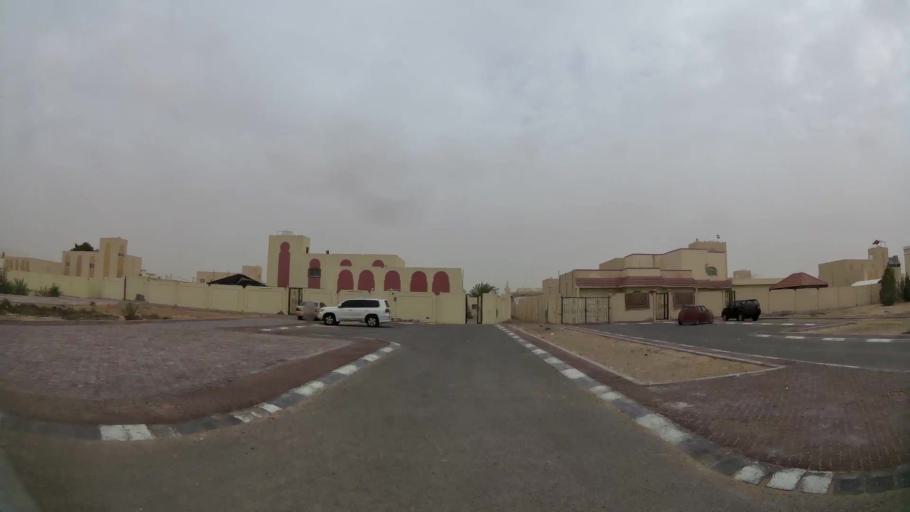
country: AE
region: Abu Dhabi
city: Abu Dhabi
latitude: 24.3762
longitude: 54.7042
